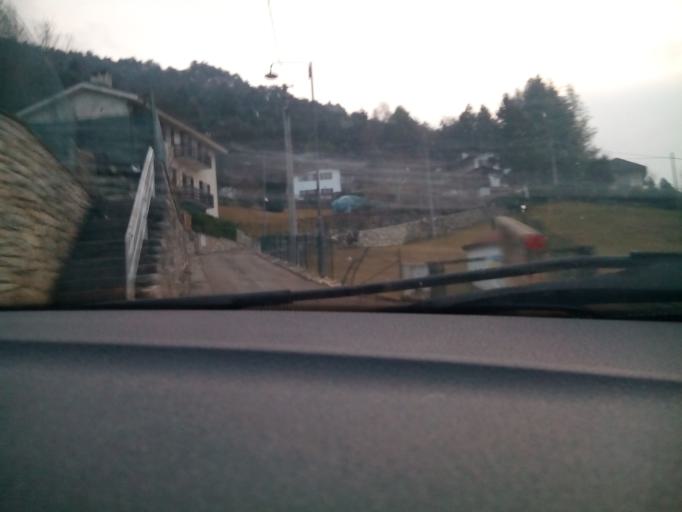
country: IT
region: Trentino-Alto Adige
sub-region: Provincia di Trento
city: Povo
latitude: 46.0490
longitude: 11.1459
